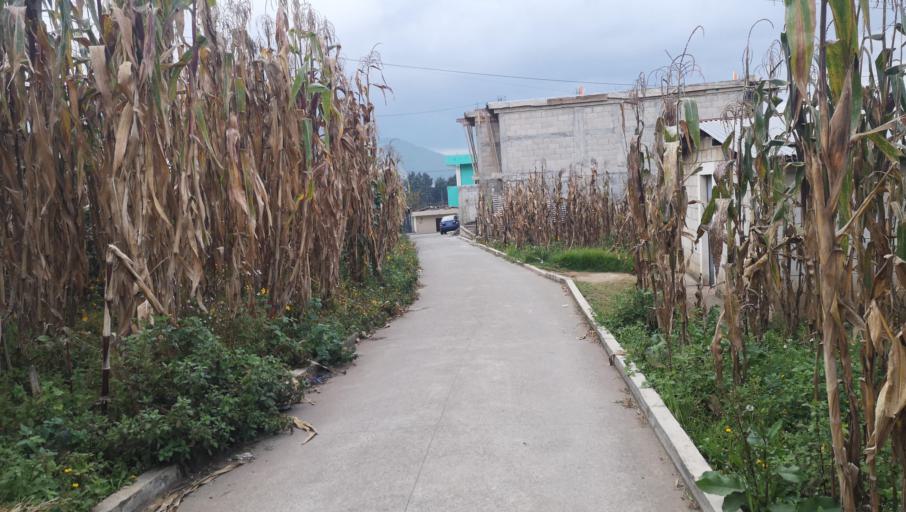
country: GT
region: Quetzaltenango
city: Cantel
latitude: 14.8194
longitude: -91.4357
